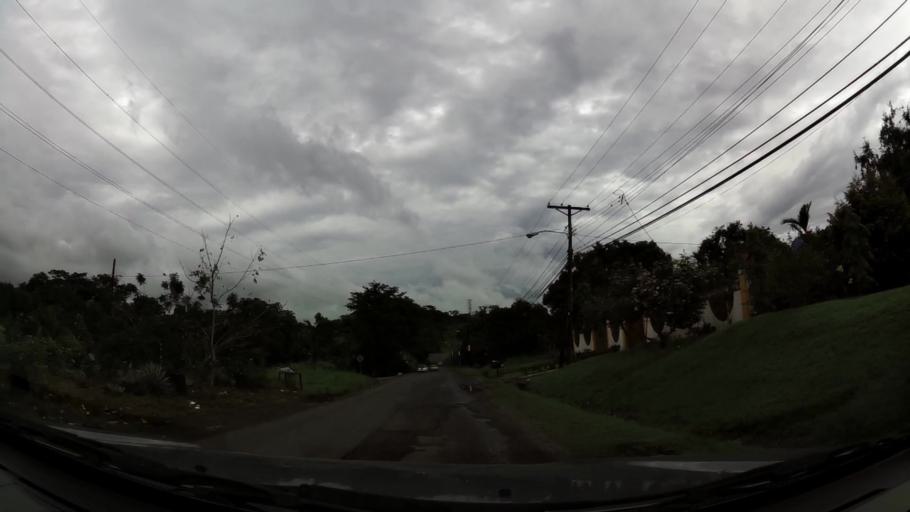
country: PA
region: Panama
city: Chilibre
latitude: 9.1640
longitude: -79.6166
